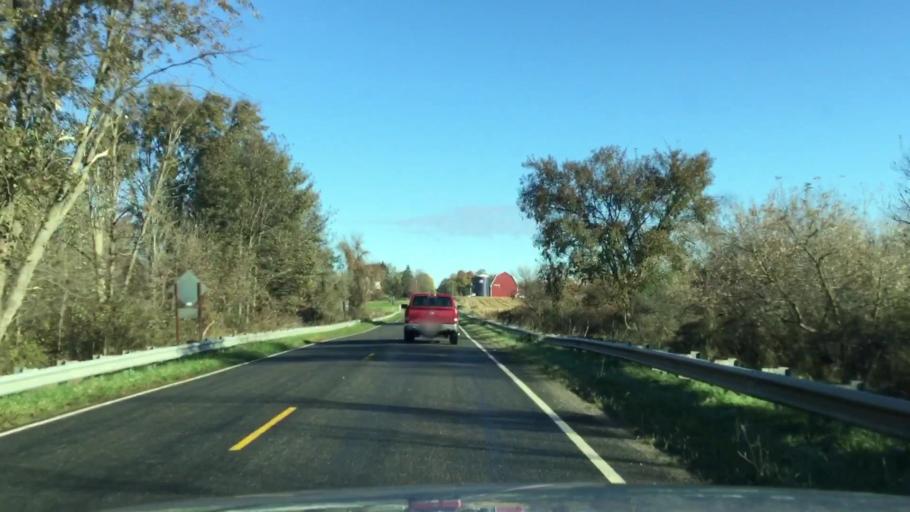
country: US
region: Michigan
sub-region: Shiawassee County
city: Durand
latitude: 42.8319
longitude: -83.9448
